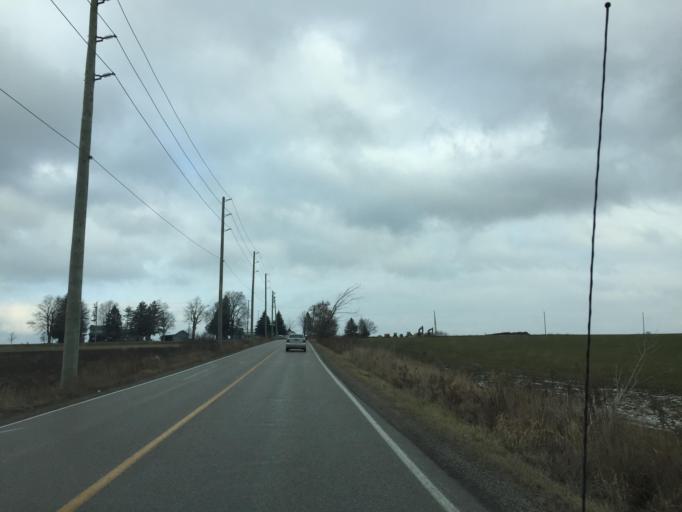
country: CA
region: Ontario
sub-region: Wellington County
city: Guelph
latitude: 43.5021
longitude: -80.3437
